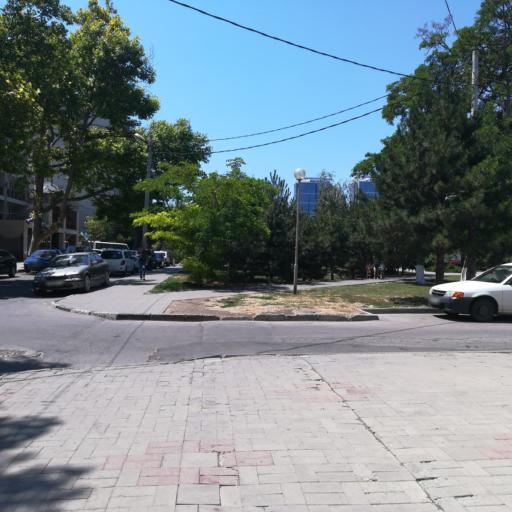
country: RU
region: Krasnodarskiy
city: Anapa
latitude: 44.8934
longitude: 37.3110
